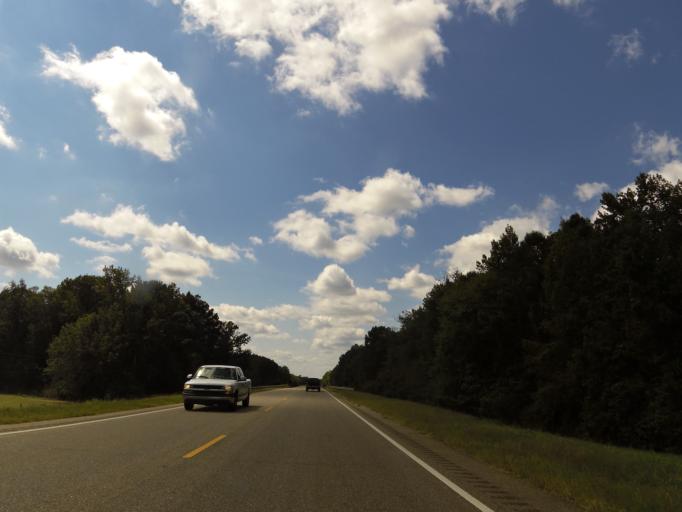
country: US
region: Alabama
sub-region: Dallas County
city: Selma
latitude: 32.3729
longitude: -87.1006
